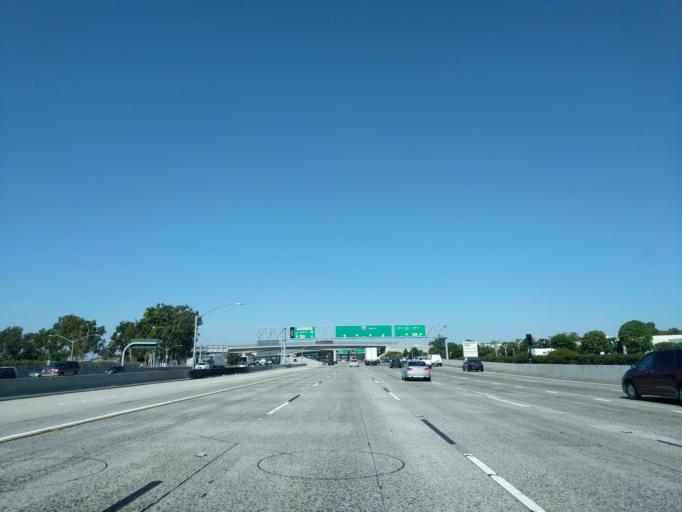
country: US
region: California
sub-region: Orange County
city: Irvine
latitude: 33.6854
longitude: -117.8627
